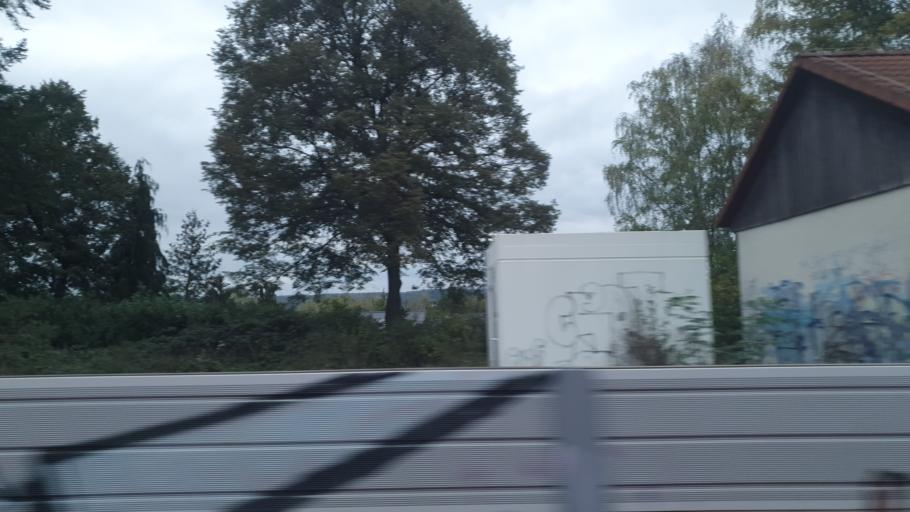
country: DE
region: Saarland
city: Sankt Ingbert
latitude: 49.2770
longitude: 7.1567
